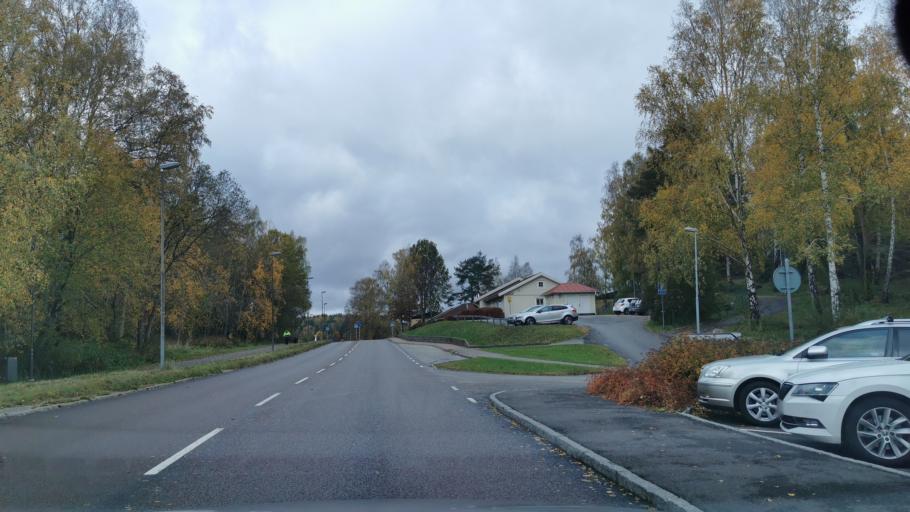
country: SE
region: Vaestra Goetaland
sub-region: Partille Kommun
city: Partille
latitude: 57.7165
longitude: 12.0727
